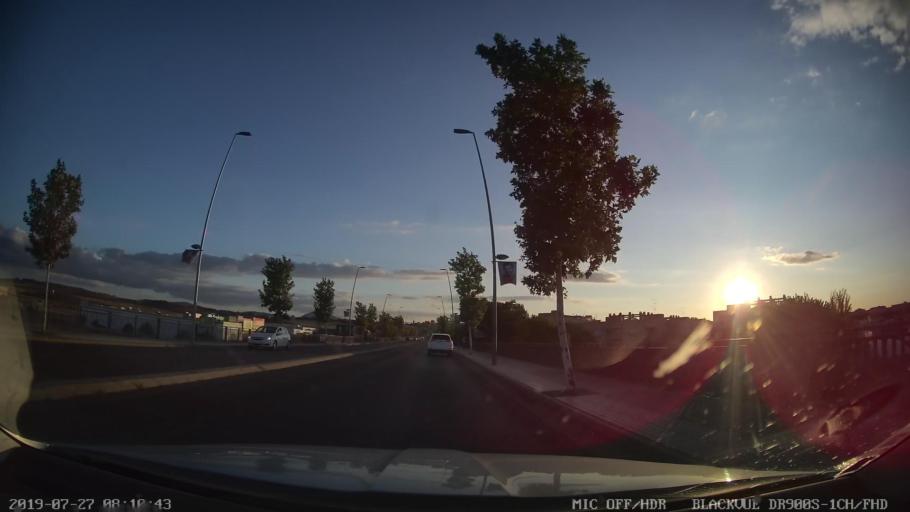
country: ES
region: Extremadura
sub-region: Provincia de Badajoz
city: Merida
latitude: 38.9080
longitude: -6.3497
